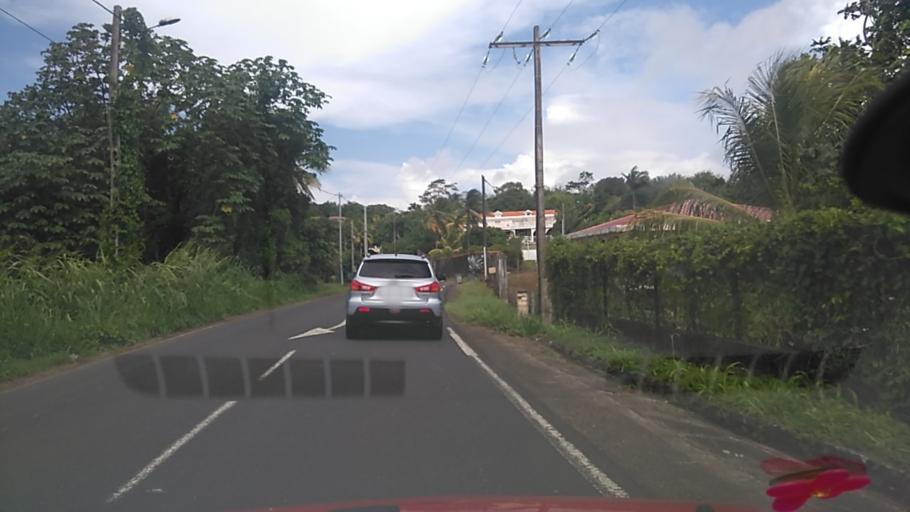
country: MQ
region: Martinique
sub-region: Martinique
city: Le Francois
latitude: 14.5996
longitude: -60.9328
